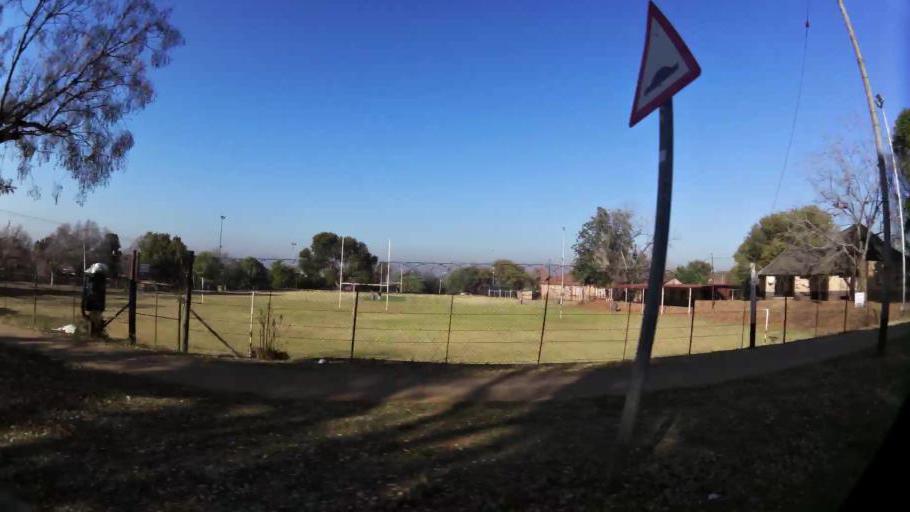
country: ZA
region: Gauteng
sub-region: City of Tshwane Metropolitan Municipality
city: Pretoria
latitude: -25.6987
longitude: 28.1679
